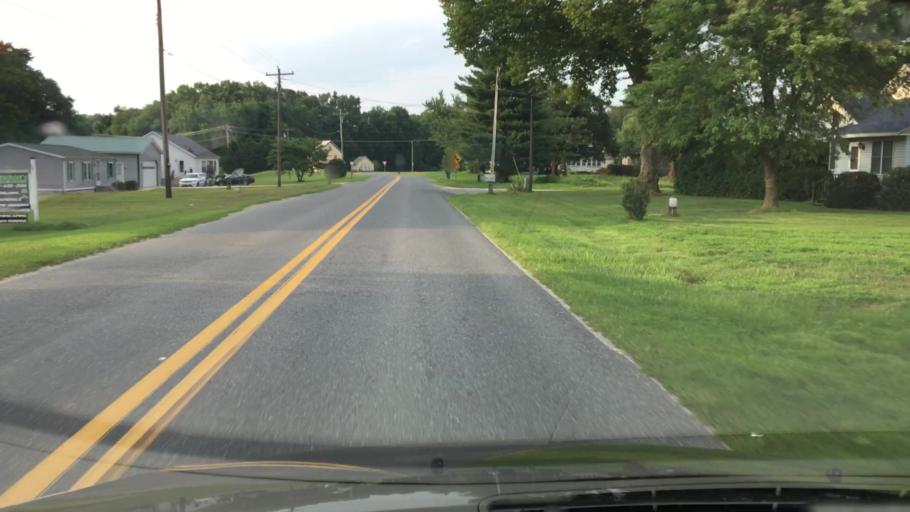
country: US
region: Maryland
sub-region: Worcester County
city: Ocean Pines
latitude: 38.4732
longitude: -75.1395
